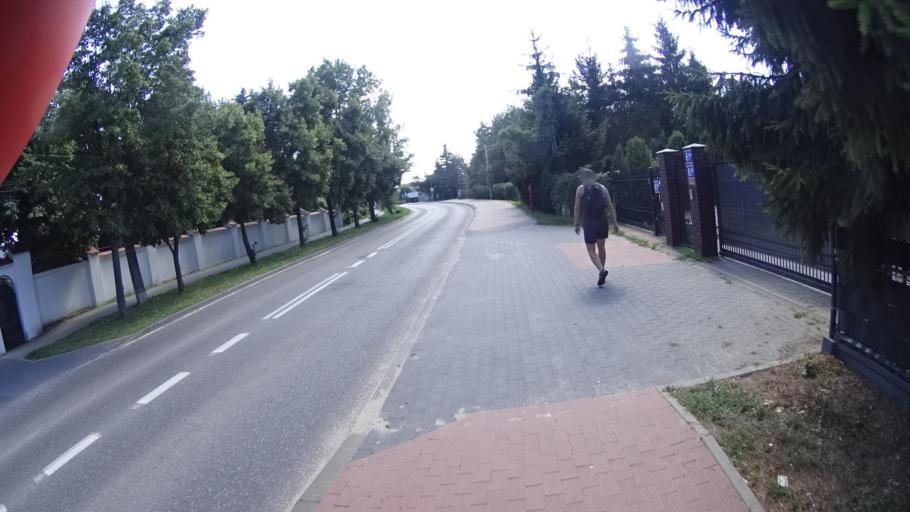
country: PL
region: Masovian Voivodeship
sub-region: Powiat piaseczynski
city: Jozefoslaw
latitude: 52.0947
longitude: 21.0520
